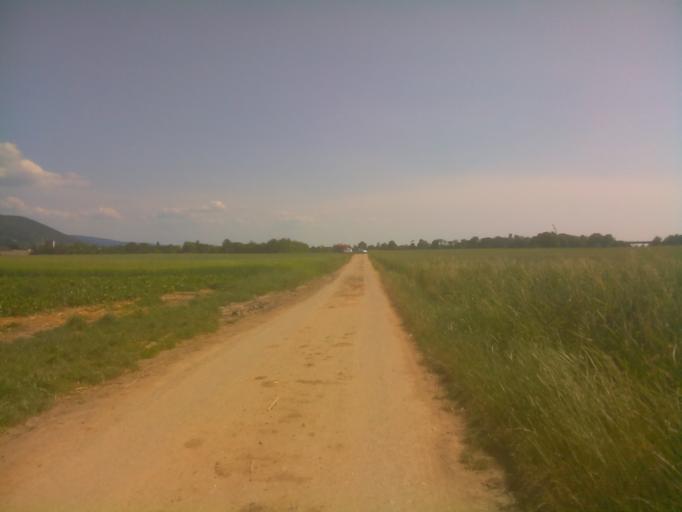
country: DE
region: Baden-Wuerttemberg
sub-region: Karlsruhe Region
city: Schriesheim
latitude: 49.5064
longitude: 8.6440
